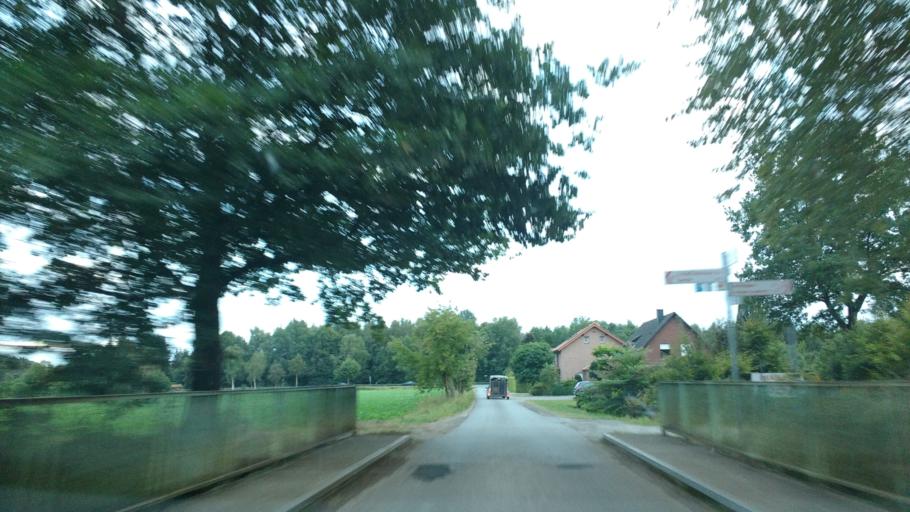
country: DE
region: North Rhine-Westphalia
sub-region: Regierungsbezirk Detmold
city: Delbruck
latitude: 51.7646
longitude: 8.6042
